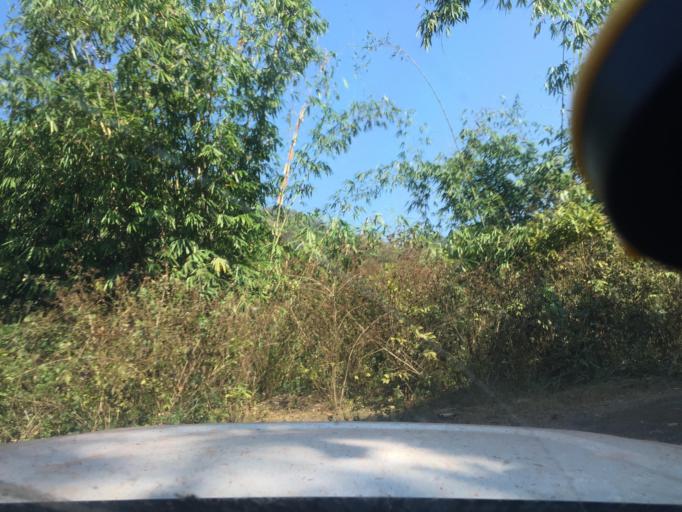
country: LA
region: Phongsali
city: Phongsali
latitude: 21.7057
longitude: 102.4002
